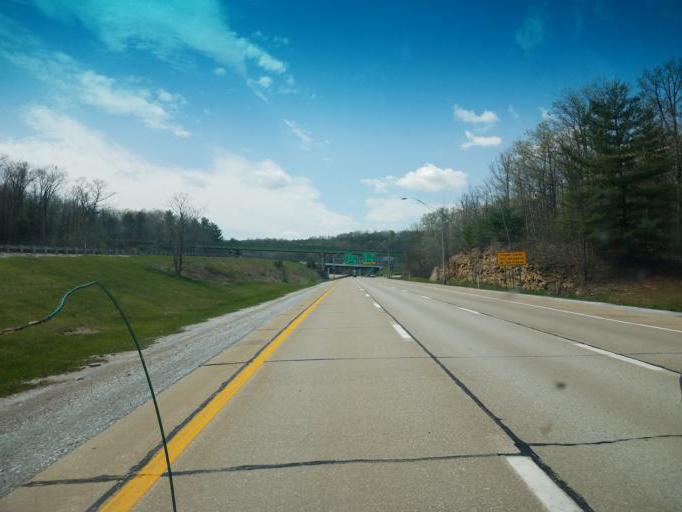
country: US
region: West Virginia
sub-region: Raleigh County
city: MacArthur
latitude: 37.7341
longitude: -81.1921
